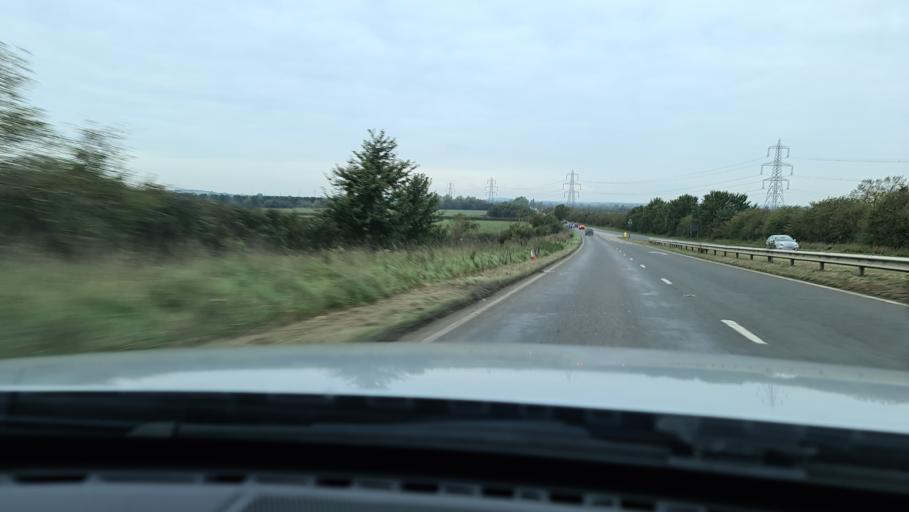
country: GB
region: England
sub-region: Buckinghamshire
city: Steeple Claydon
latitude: 51.8693
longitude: -1.0120
